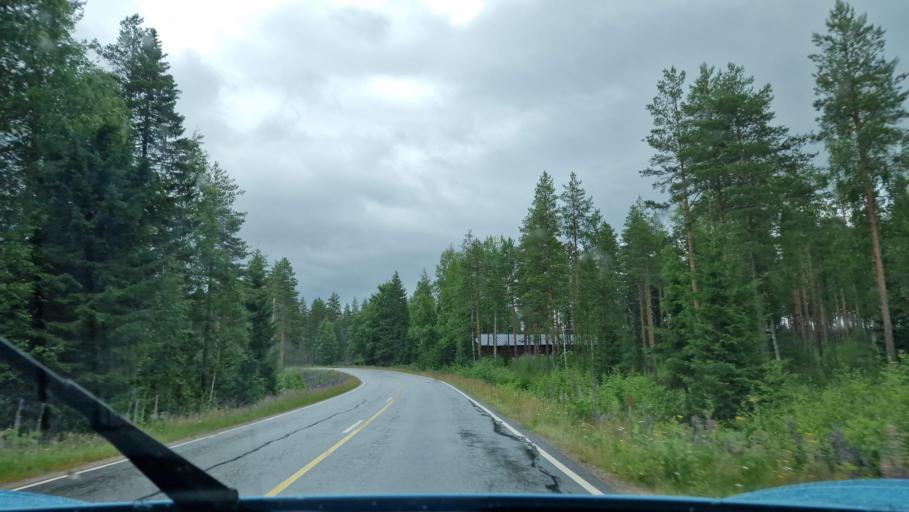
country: FI
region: Southern Ostrobothnia
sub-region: Jaerviseutu
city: Soini
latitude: 62.7755
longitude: 24.3882
